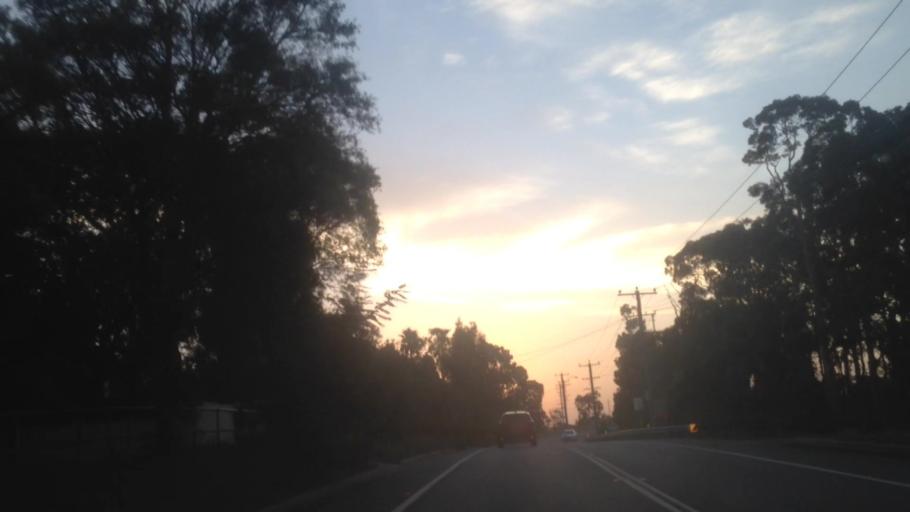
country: AU
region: New South Wales
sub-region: Lake Macquarie Shire
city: Dora Creek
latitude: -33.1071
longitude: 151.4951
